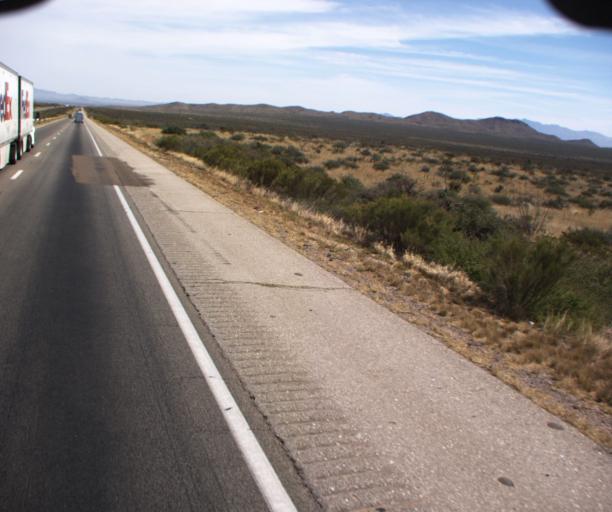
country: US
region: Arizona
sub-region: Cochise County
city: Willcox
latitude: 32.1165
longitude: -110.0194
